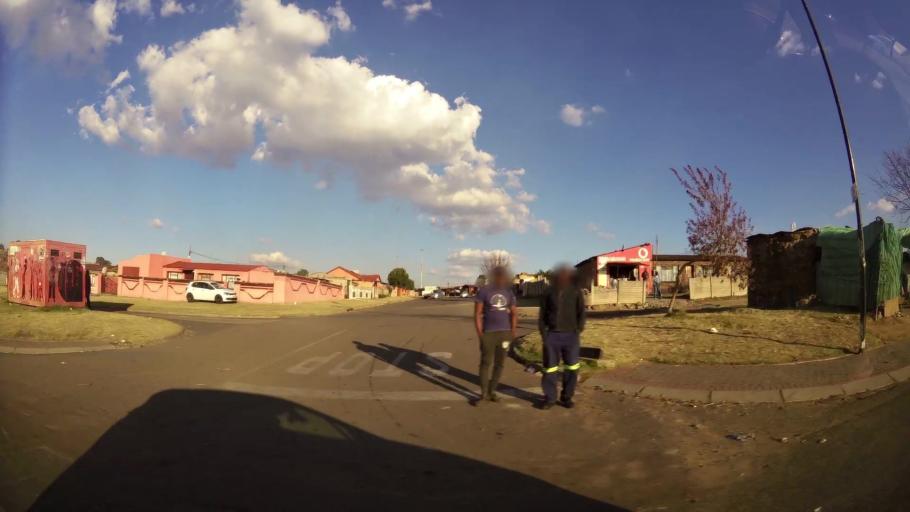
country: ZA
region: Mpumalanga
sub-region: Nkangala District Municipality
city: Witbank
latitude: -25.8782
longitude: 29.1962
